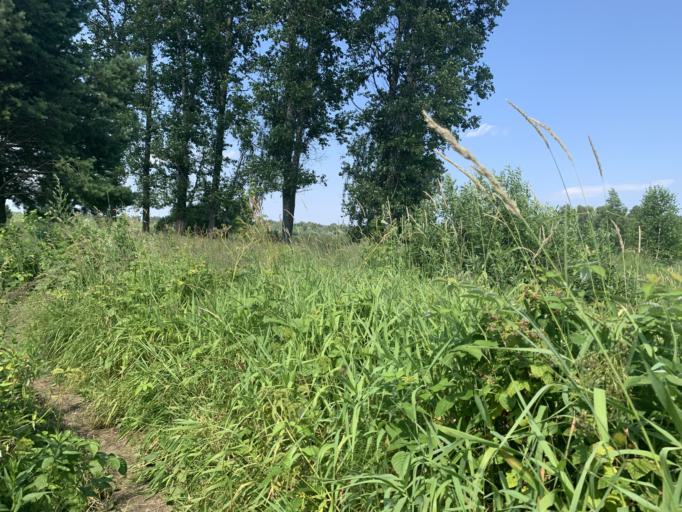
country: RU
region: Moskovskaya
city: Mamontovka
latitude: 55.9722
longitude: 37.8052
